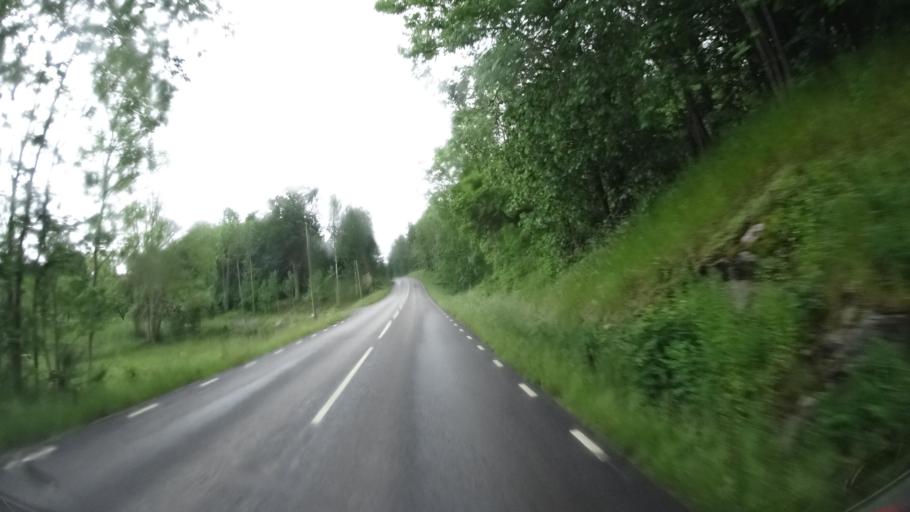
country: SE
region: Kalmar
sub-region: Oskarshamns Kommun
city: Oskarshamn
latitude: 57.3934
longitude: 16.2145
